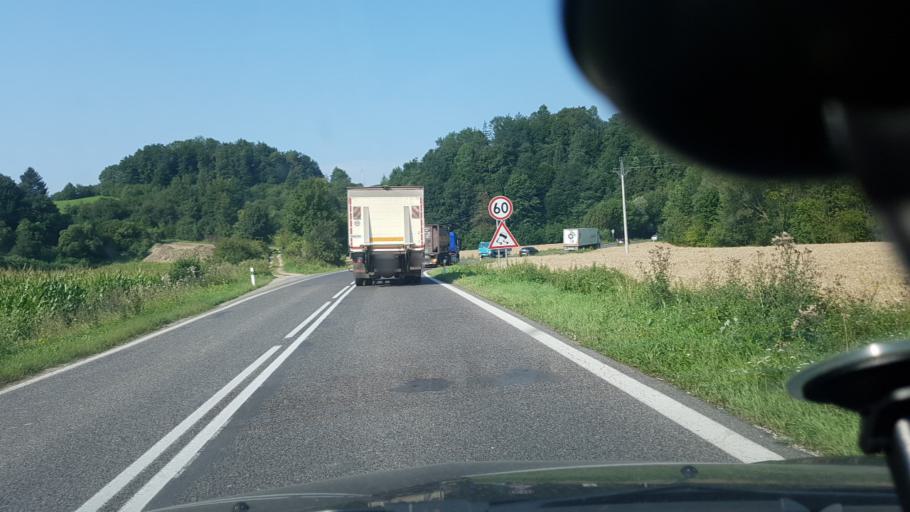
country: SK
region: Zilinsky
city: Tvrdosin
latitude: 49.2797
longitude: 19.4700
